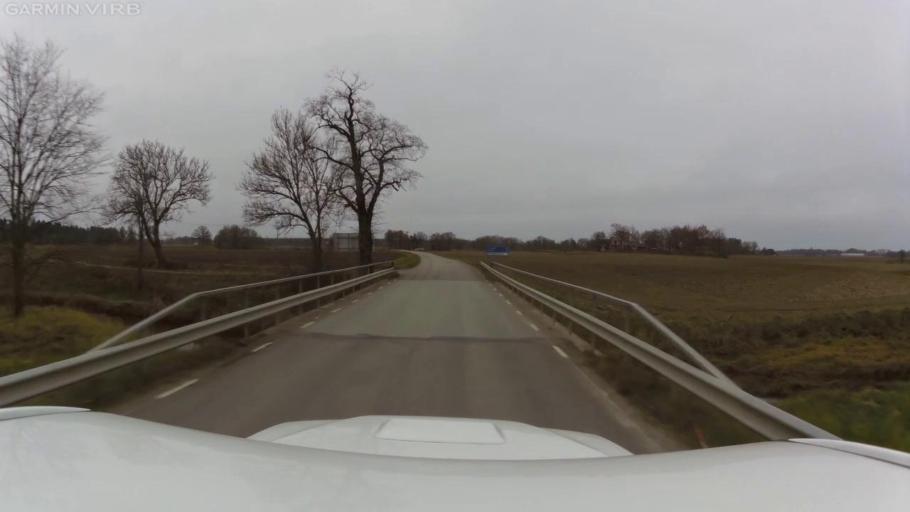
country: SE
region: OEstergoetland
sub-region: Linkopings Kommun
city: Vikingstad
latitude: 58.3741
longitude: 15.4348
